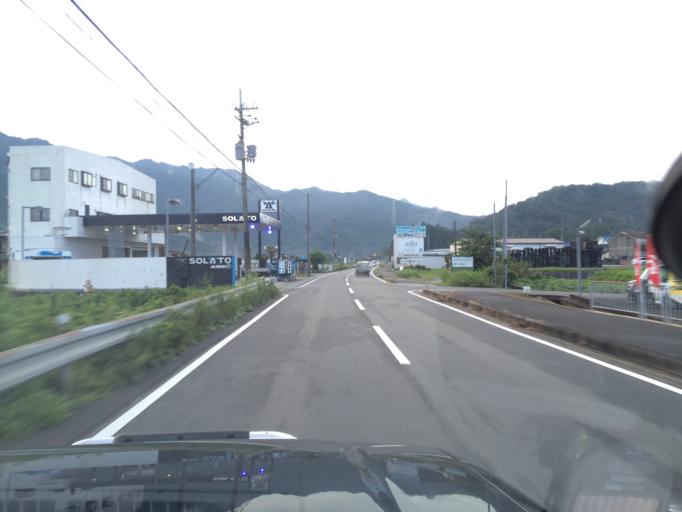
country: JP
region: Hyogo
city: Nishiwaki
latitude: 35.1061
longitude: 134.9944
